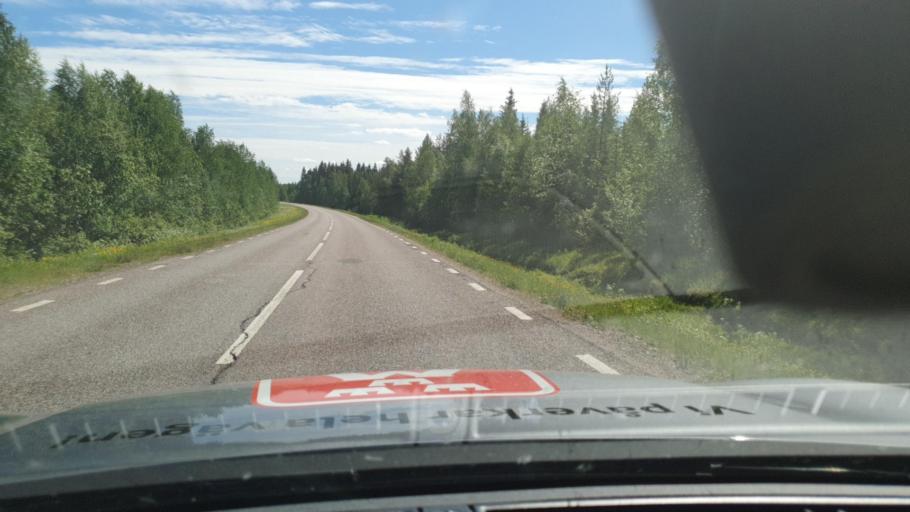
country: FI
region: Lapland
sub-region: Torniolaakso
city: Pello
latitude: 66.9207
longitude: 23.8537
